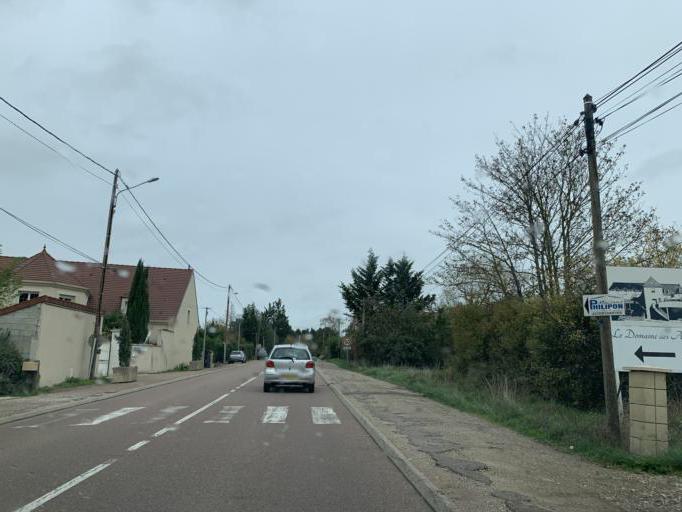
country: FR
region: Bourgogne
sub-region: Departement de l'Yonne
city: Moneteau
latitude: 47.8295
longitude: 3.5899
